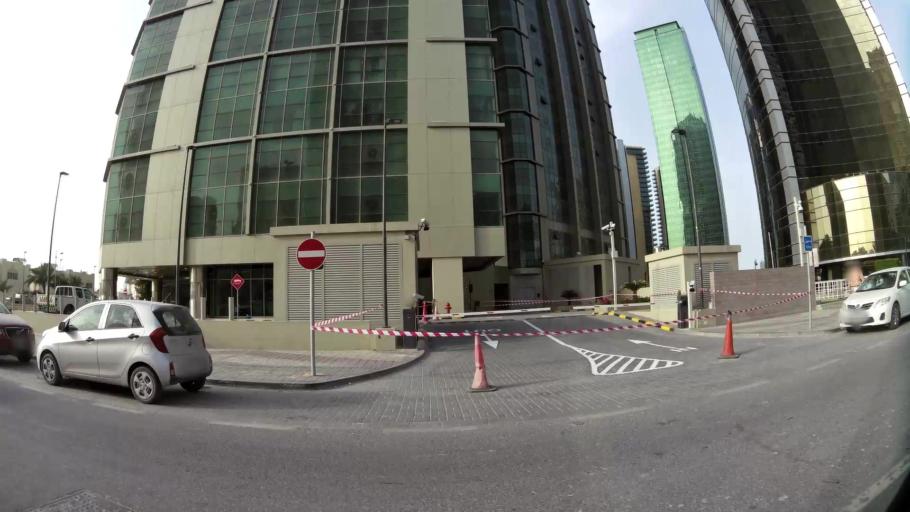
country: QA
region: Baladiyat ad Dawhah
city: Doha
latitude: 25.3274
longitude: 51.5247
